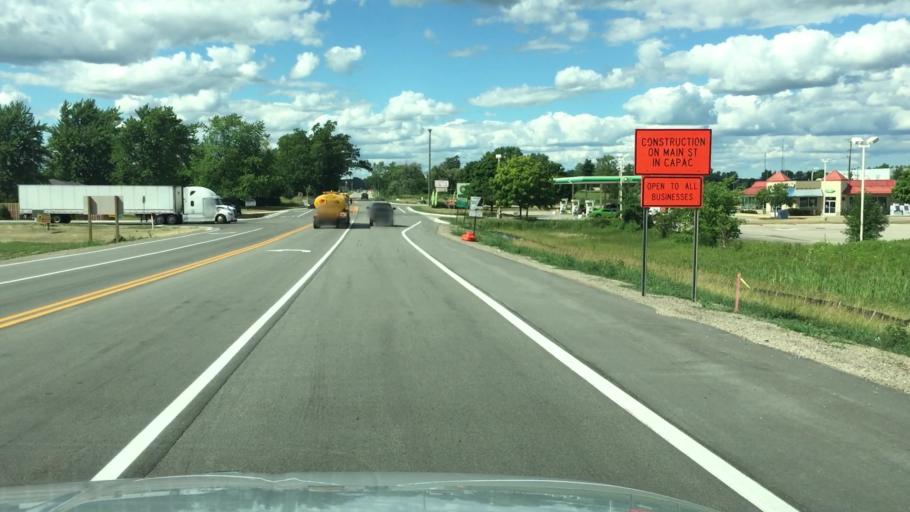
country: US
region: Michigan
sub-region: Saint Clair County
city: Capac
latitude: 42.9892
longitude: -82.9278
